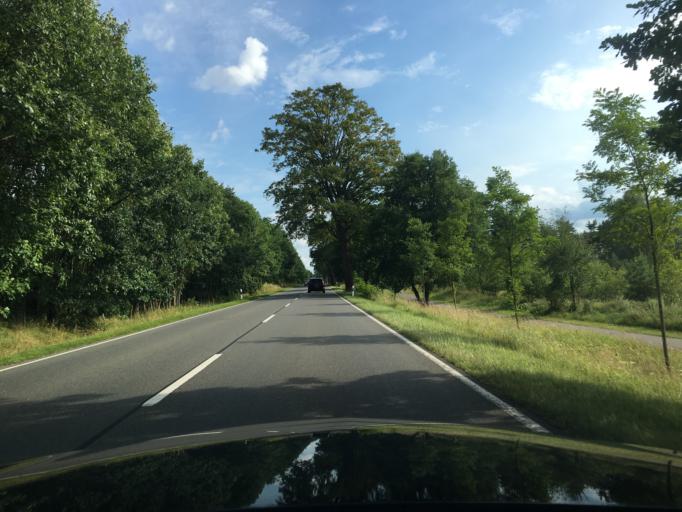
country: DE
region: Mecklenburg-Vorpommern
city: Neustrelitz
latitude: 53.4047
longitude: 13.0426
